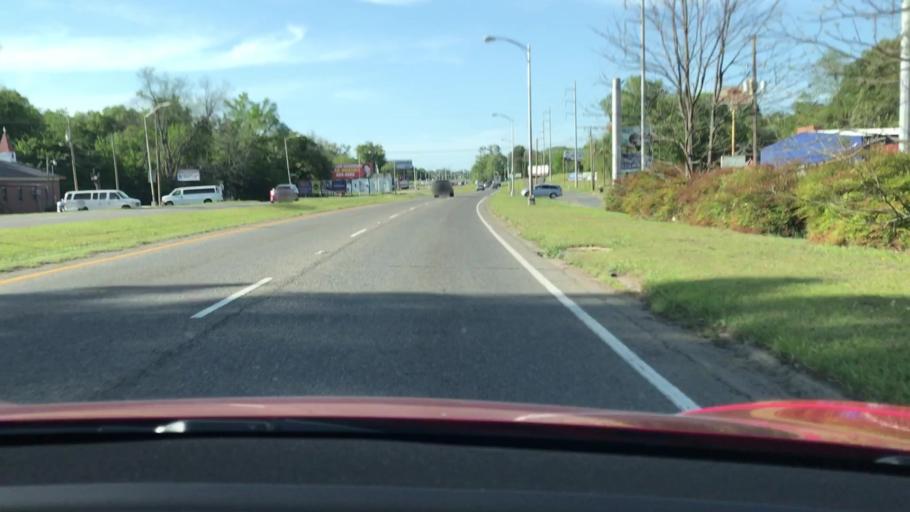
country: US
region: Louisiana
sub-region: Bossier Parish
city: Bossier City
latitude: 32.4881
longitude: -93.7242
